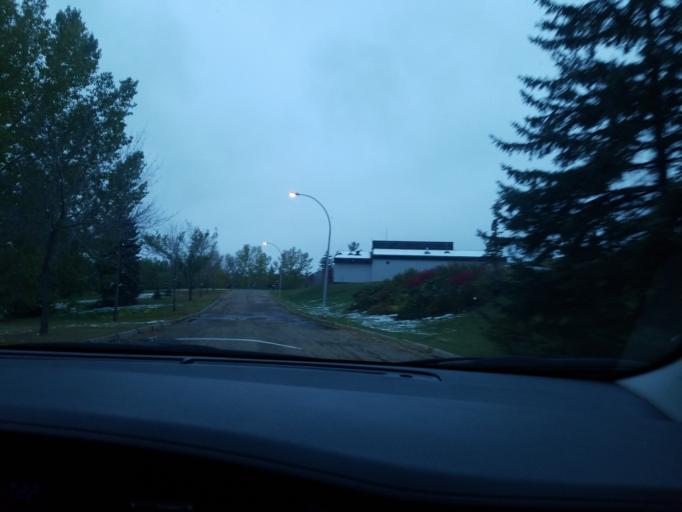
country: CA
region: Alberta
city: Edmonton
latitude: 53.5555
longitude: -113.3918
